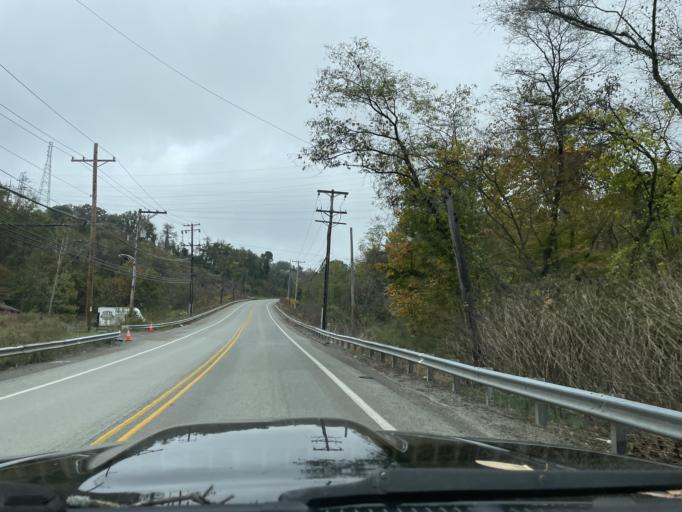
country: US
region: Pennsylvania
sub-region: Allegheny County
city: Cheswick
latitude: 40.5278
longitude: -79.7946
